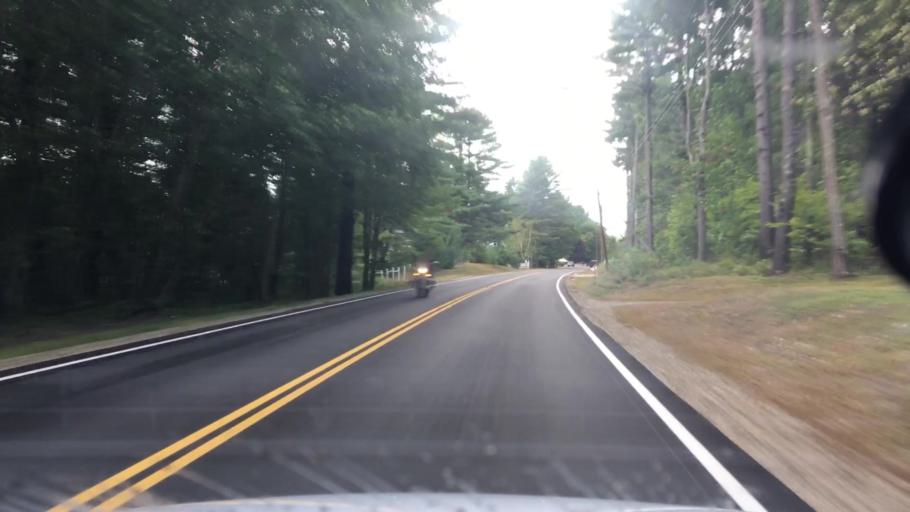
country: US
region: New Hampshire
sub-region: Carroll County
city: Sanbornville
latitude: 43.5345
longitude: -71.0246
